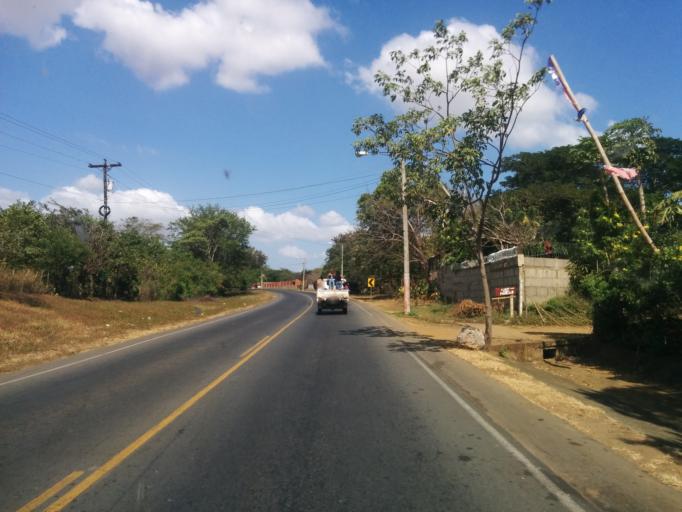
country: NI
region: Masaya
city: Nindiri
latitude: 12.0349
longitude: -86.0992
